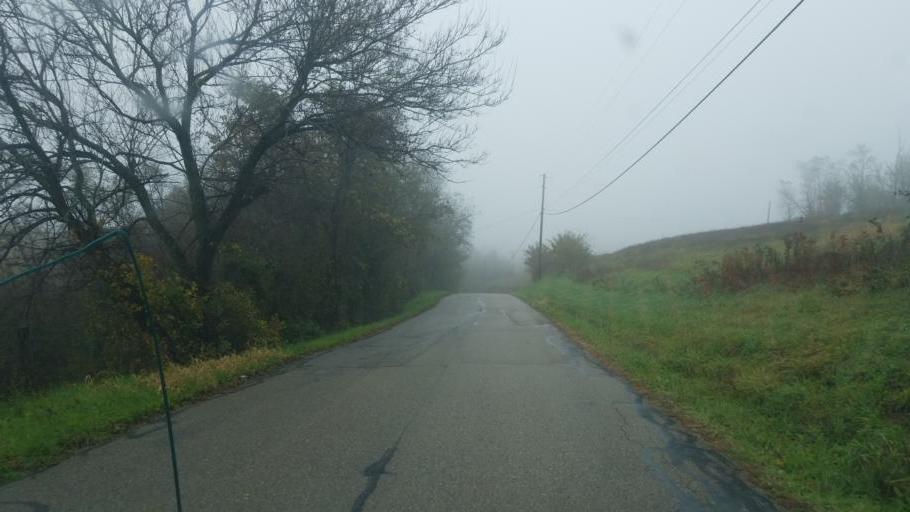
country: US
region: Ohio
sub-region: Morgan County
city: McConnelsville
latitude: 39.6333
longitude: -81.8762
